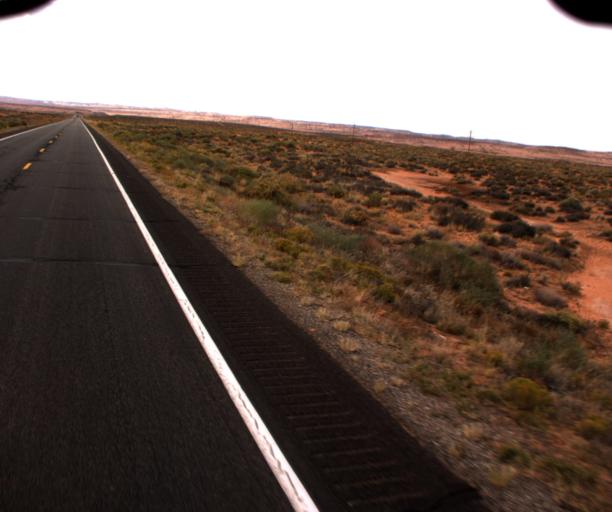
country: US
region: Arizona
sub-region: Apache County
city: Many Farms
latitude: 36.9409
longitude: -109.6625
